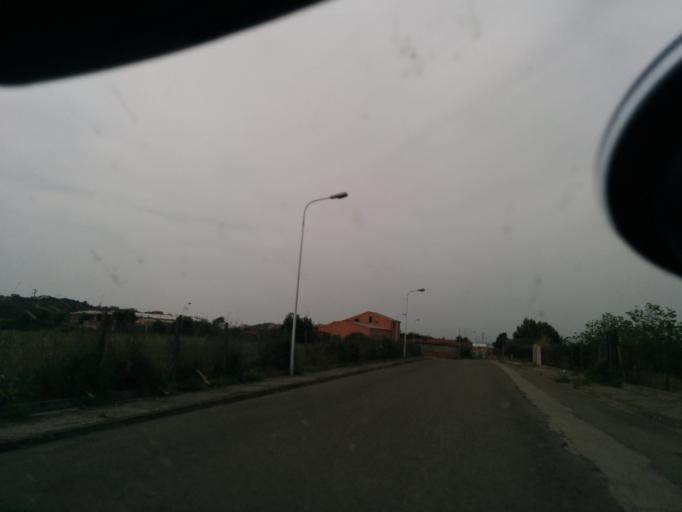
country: IT
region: Sardinia
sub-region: Provincia di Carbonia-Iglesias
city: Sant'Antioco
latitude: 39.0426
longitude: 8.4554
